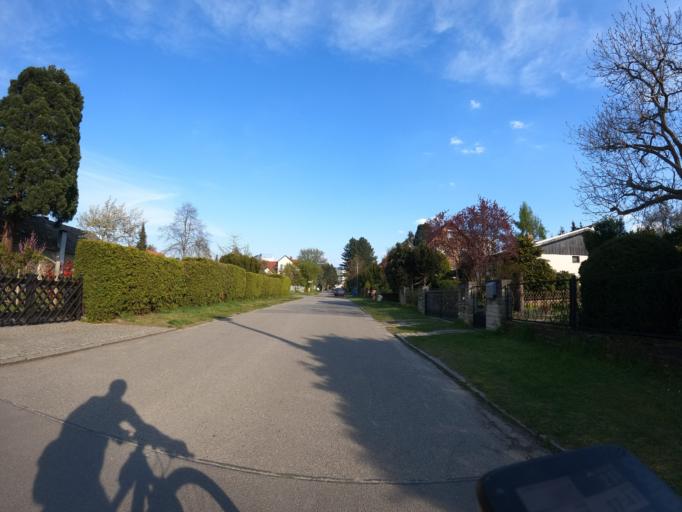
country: DE
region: Berlin
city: Marzahn
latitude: 52.5376
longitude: 13.5472
